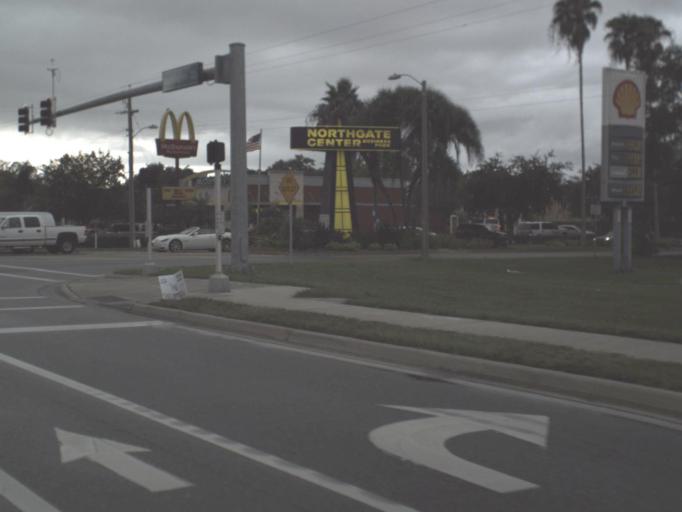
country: US
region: Florida
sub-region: Sarasota County
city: North Sarasota
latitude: 27.3725
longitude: -82.5310
